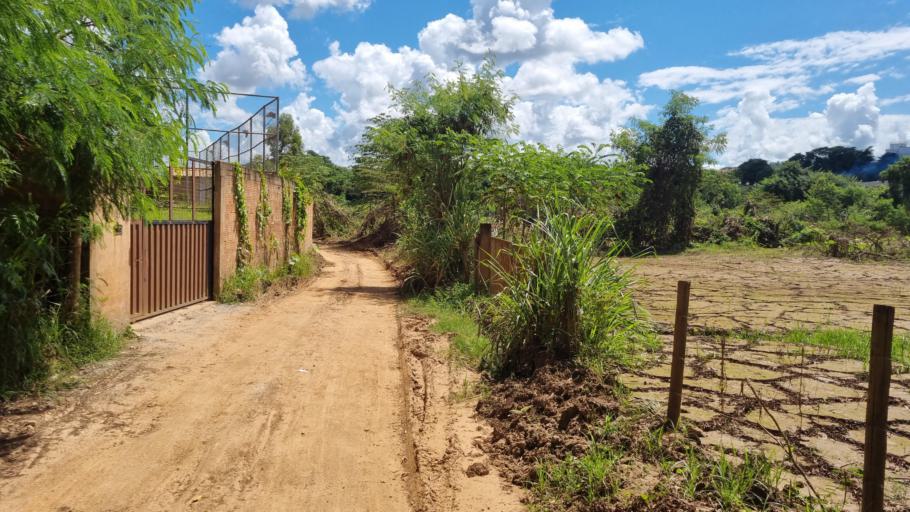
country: BR
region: Minas Gerais
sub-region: Santa Luzia
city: Santa Luzia
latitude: -19.8358
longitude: -43.8649
